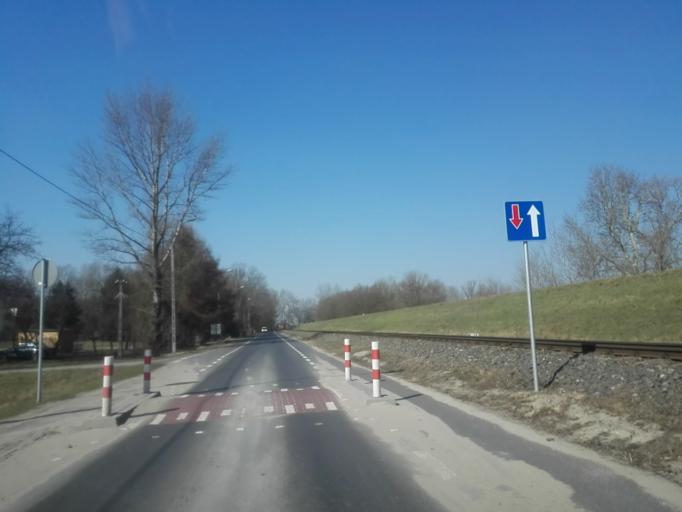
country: PL
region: Masovian Voivodeship
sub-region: Warszawa
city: Wilanow
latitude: 52.1656
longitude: 21.1278
